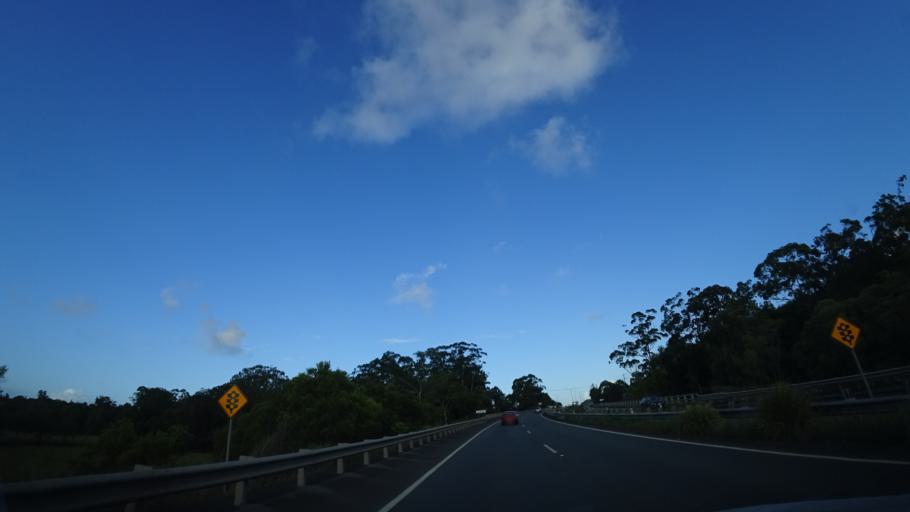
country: AU
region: Queensland
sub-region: Sunshine Coast
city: Buderim
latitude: -26.6620
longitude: 153.0308
